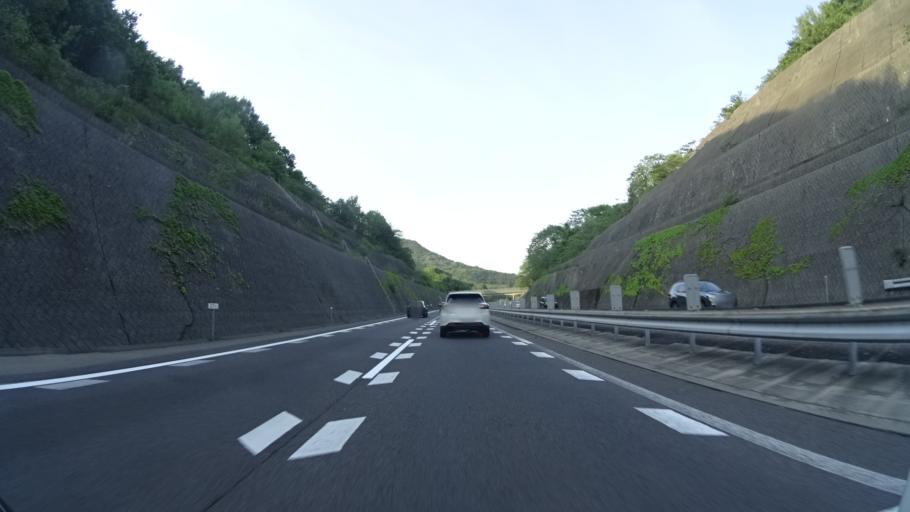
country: JP
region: Kagawa
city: Tadotsu
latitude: 34.2217
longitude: 133.7307
